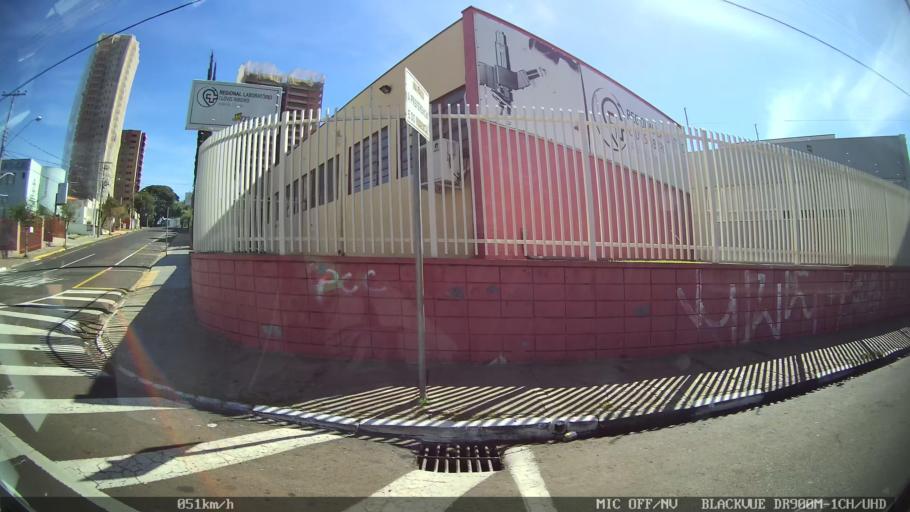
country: BR
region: Sao Paulo
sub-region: Franca
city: Franca
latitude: -20.5395
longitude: -47.3935
